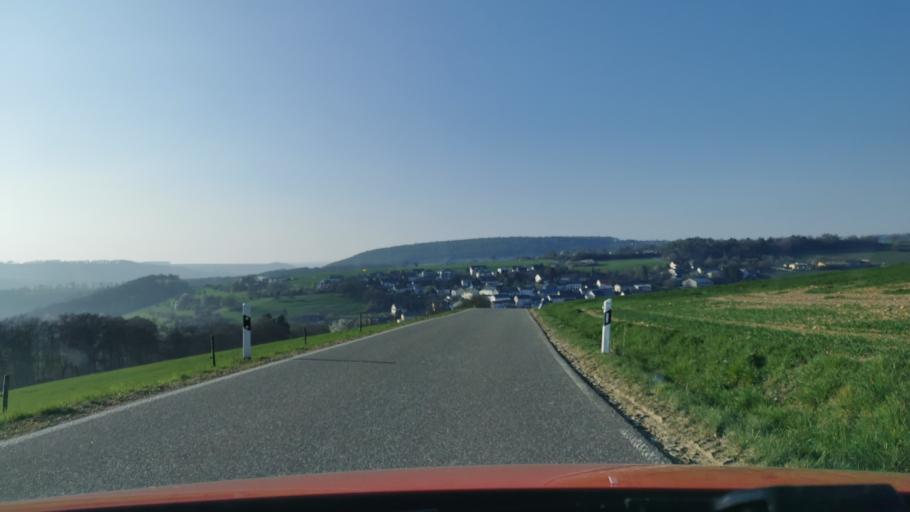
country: DE
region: Rheinland-Pfalz
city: Trierweiler
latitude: 49.7706
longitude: 6.5510
